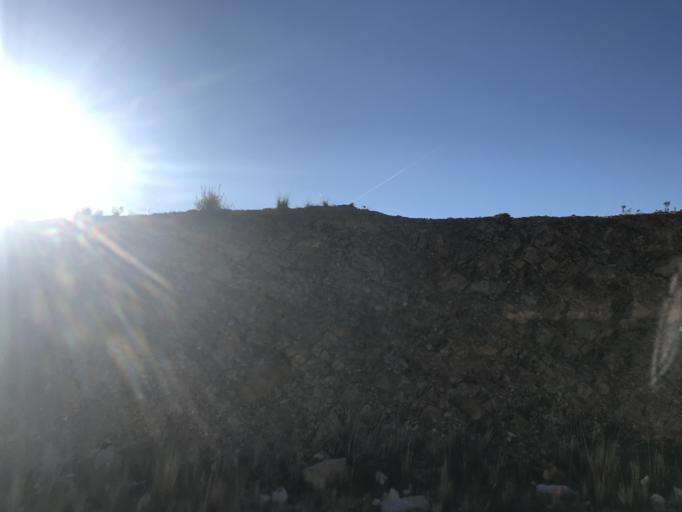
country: BO
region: La Paz
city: San Pablo
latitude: -16.2041
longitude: -68.8329
